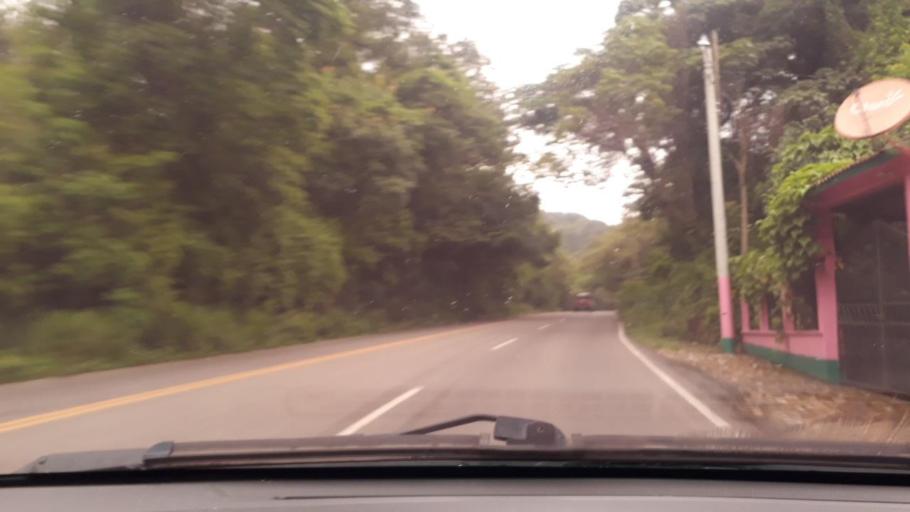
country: GT
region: Chiquimula
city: Esquipulas
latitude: 14.5542
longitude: -89.3762
